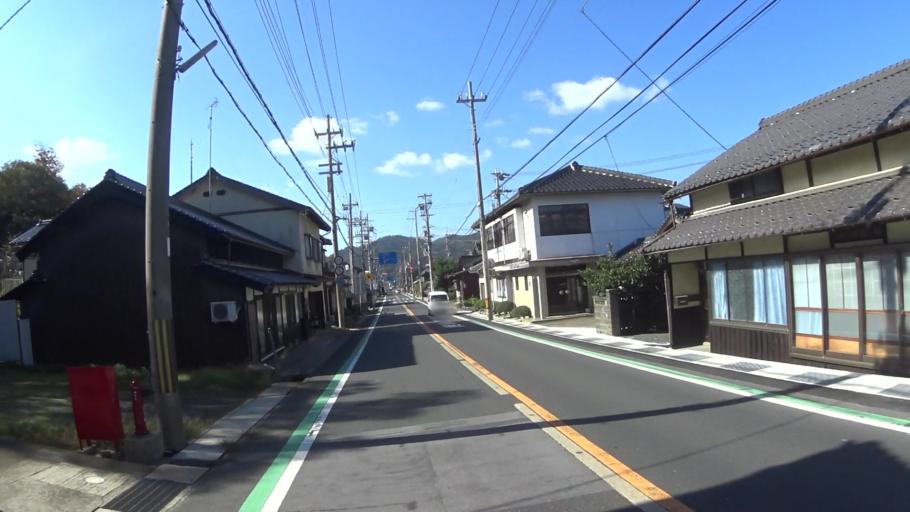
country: JP
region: Kyoto
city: Miyazu
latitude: 35.6816
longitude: 135.0328
